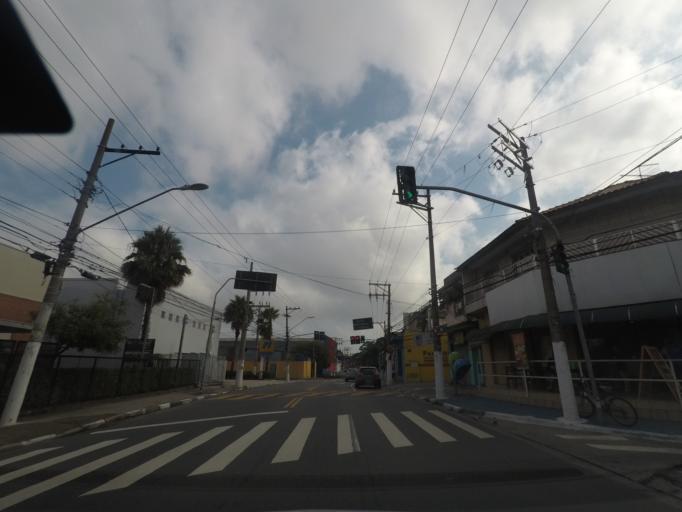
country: BR
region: Sao Paulo
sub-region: Osasco
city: Osasco
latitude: -23.5584
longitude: -46.7816
